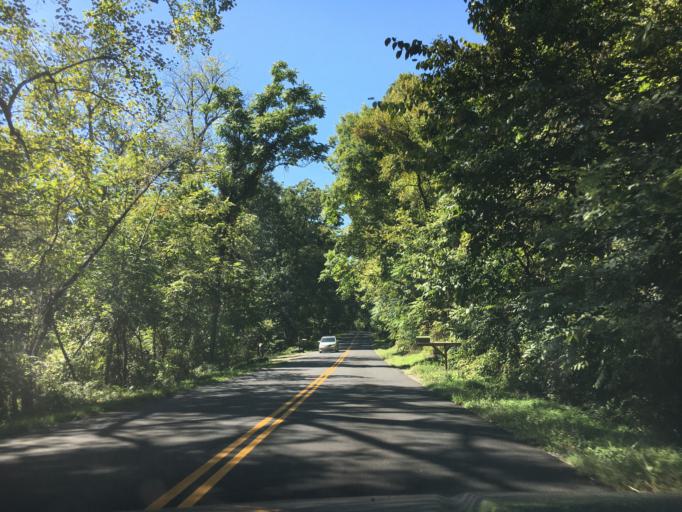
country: US
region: Virginia
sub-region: Albemarle County
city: Crozet
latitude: 37.9798
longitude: -78.7000
